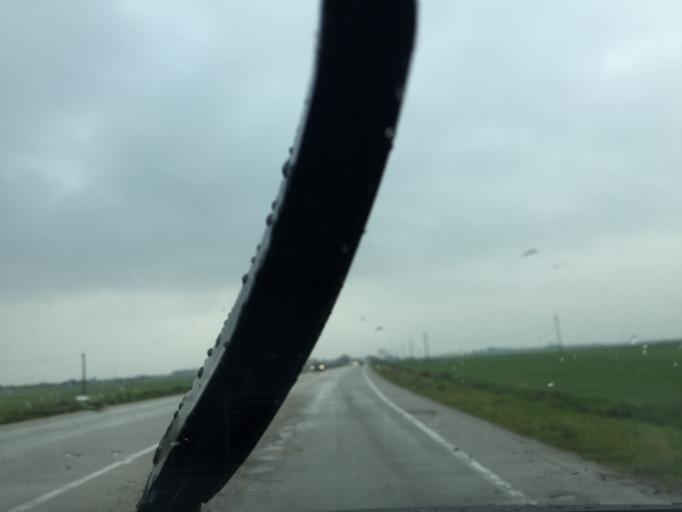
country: IT
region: Apulia
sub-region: Provincia di Foggia
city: Foggia
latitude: 41.4847
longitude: 15.5207
